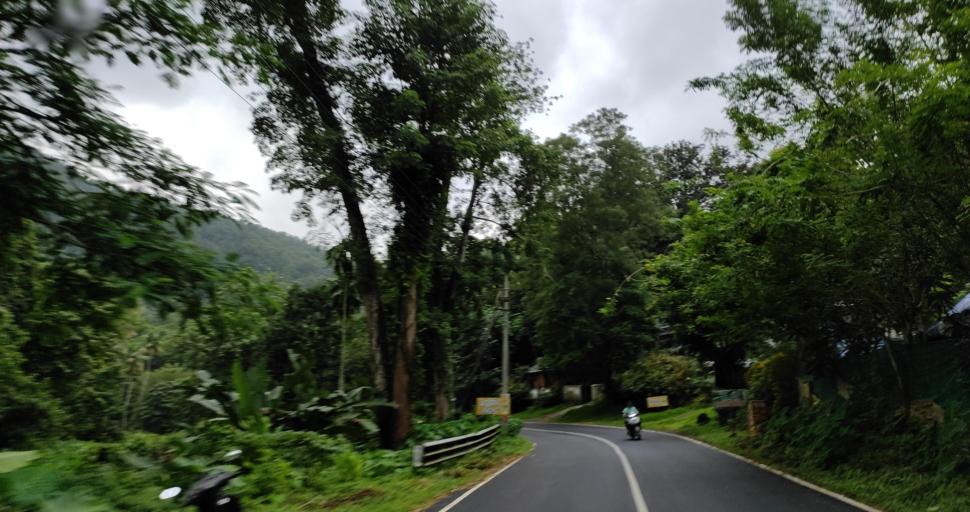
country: IN
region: Kerala
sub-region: Thrissur District
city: Kizhake Chalakudi
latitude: 10.3007
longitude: 76.4500
